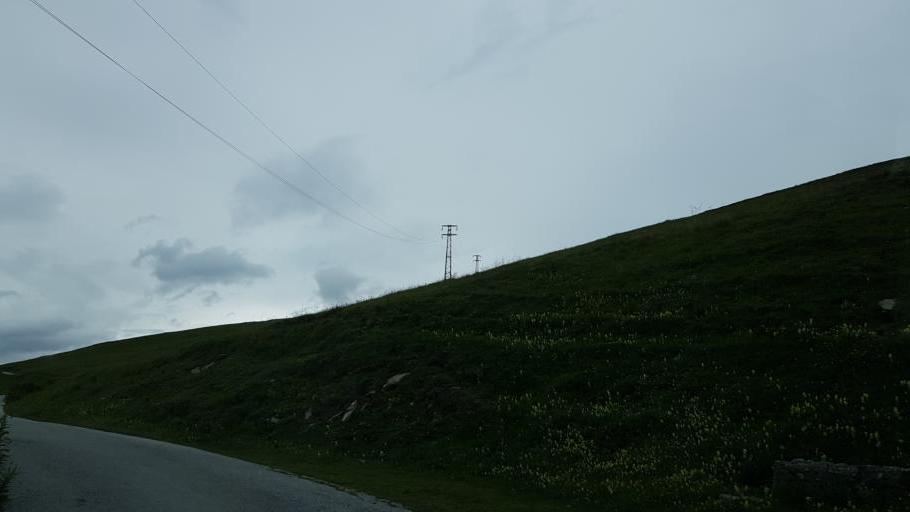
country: IT
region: Piedmont
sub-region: Provincia di Cuneo
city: Serre
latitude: 44.5469
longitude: 7.1213
